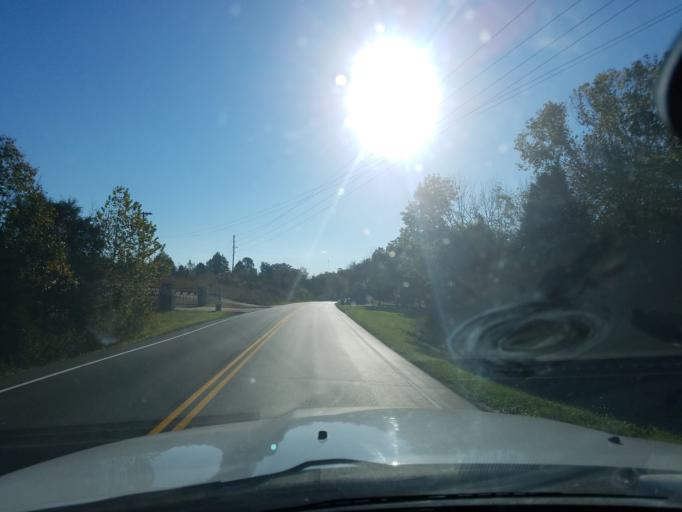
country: US
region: Kentucky
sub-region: Nelson County
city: Bardstown
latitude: 37.7864
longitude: -85.4053
